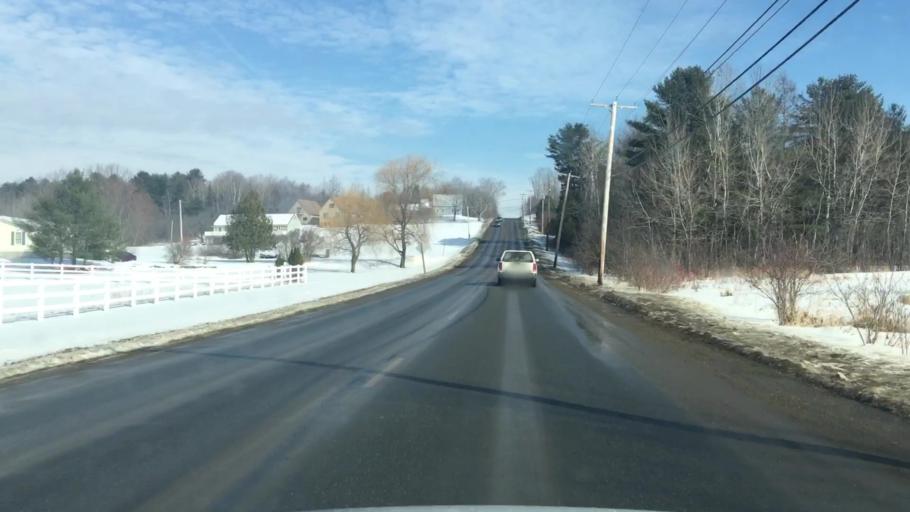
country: US
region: Maine
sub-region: Penobscot County
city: Hermon
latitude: 44.8307
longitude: -68.8828
